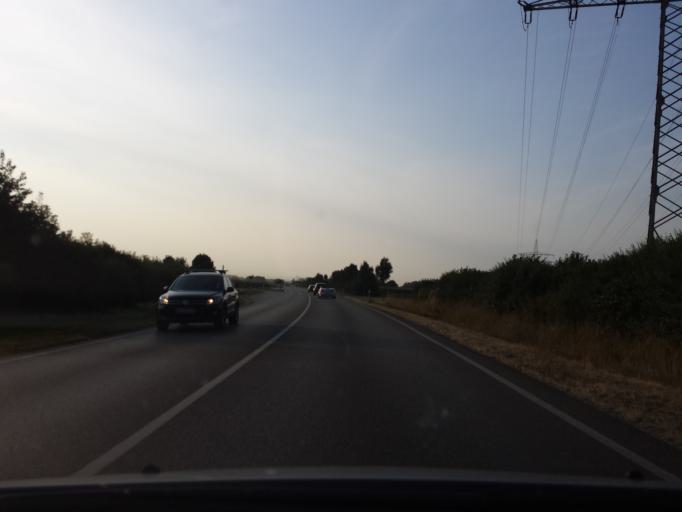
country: DE
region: Bavaria
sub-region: Swabia
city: Friedberg
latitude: 48.3833
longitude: 10.9599
